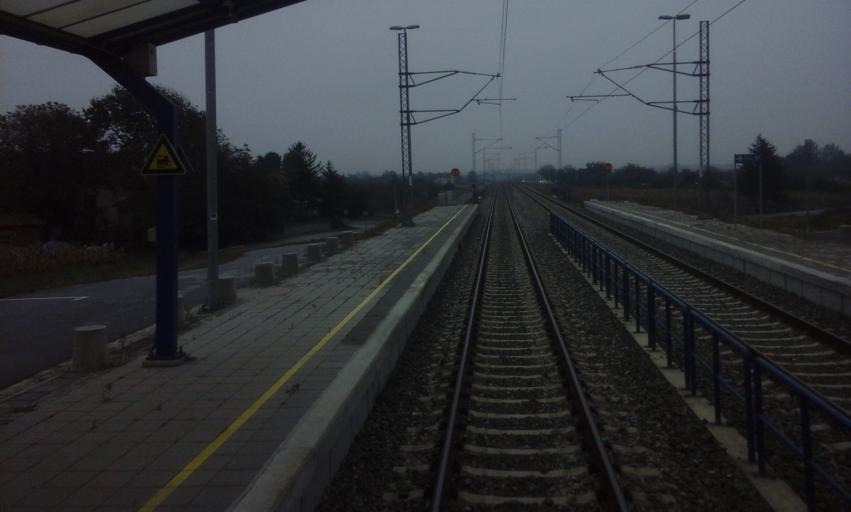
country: RS
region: Central Serbia
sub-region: Pomoravski Okrug
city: Cuprija
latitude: 43.9542
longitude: 21.3178
